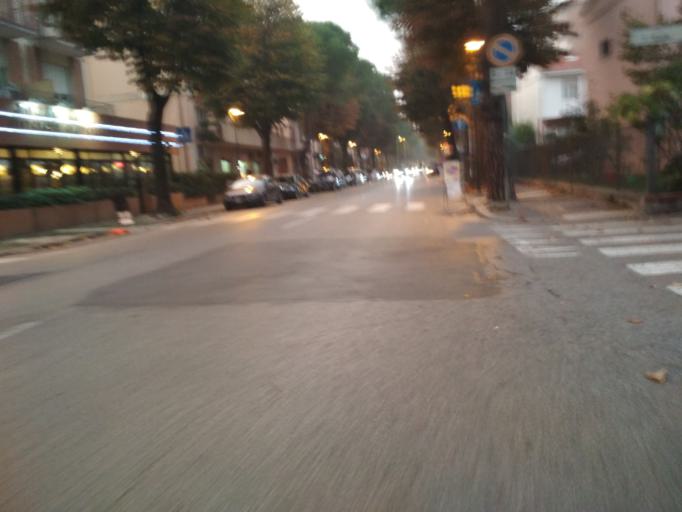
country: IT
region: Emilia-Romagna
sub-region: Provincia di Rimini
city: Rimini
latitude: 44.0685
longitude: 12.5683
